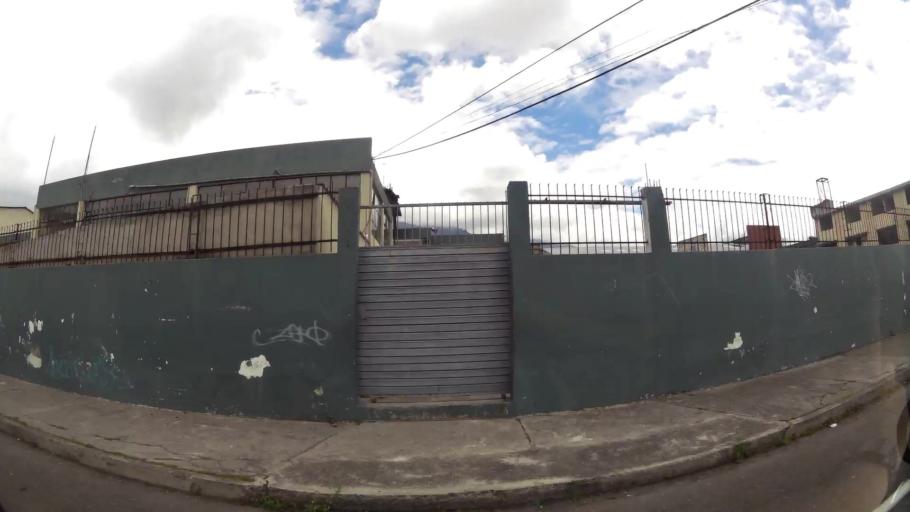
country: EC
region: Pichincha
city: Quito
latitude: -0.1686
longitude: -78.4835
